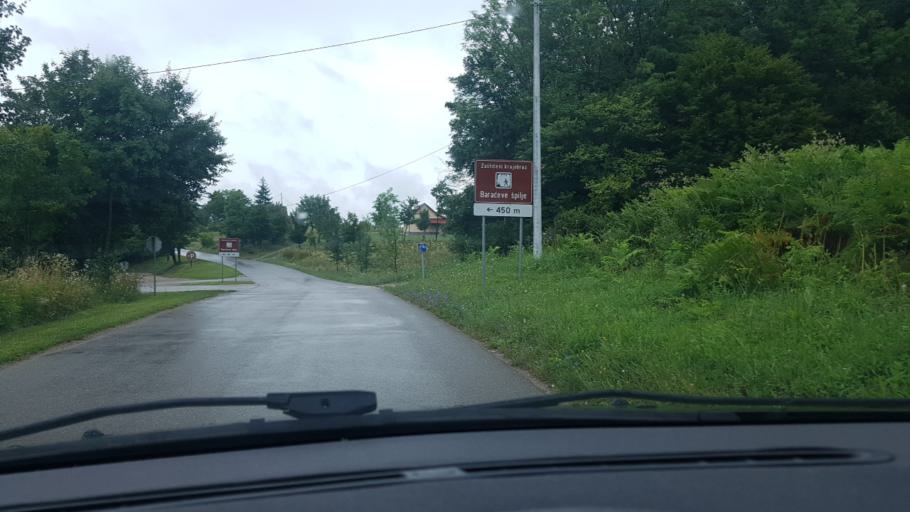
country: BA
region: Federation of Bosnia and Herzegovina
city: Trzacka Rastela
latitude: 44.9857
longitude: 15.7292
